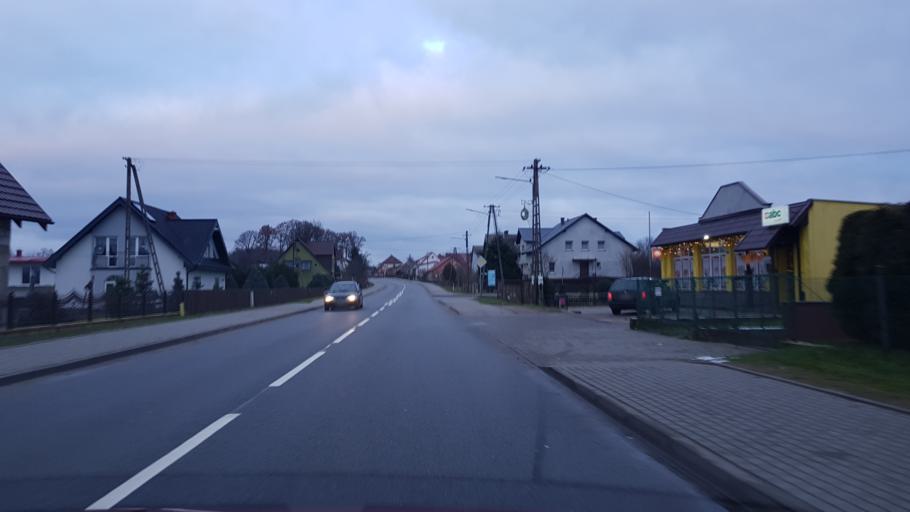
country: PL
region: Pomeranian Voivodeship
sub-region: Powiat bytowski
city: Tuchomie
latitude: 54.0560
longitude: 17.2380
